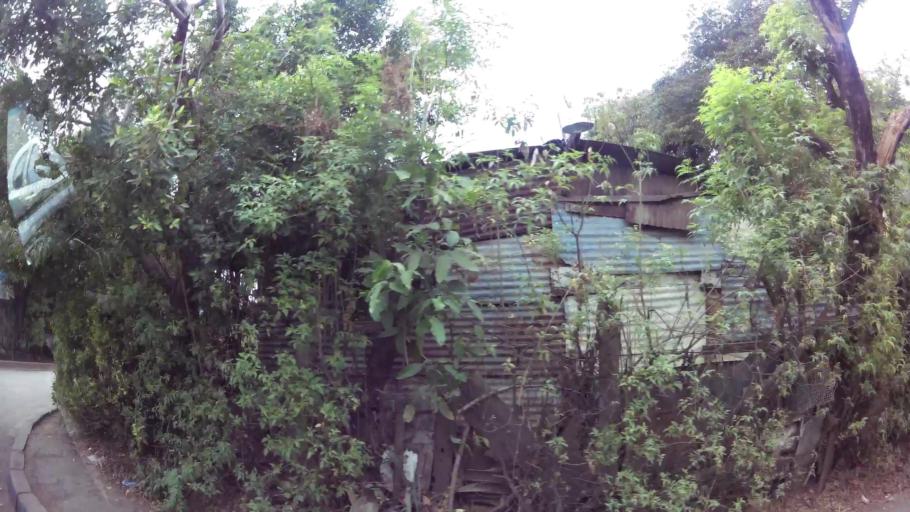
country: NI
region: Managua
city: Managua
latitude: 12.1131
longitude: -86.2170
